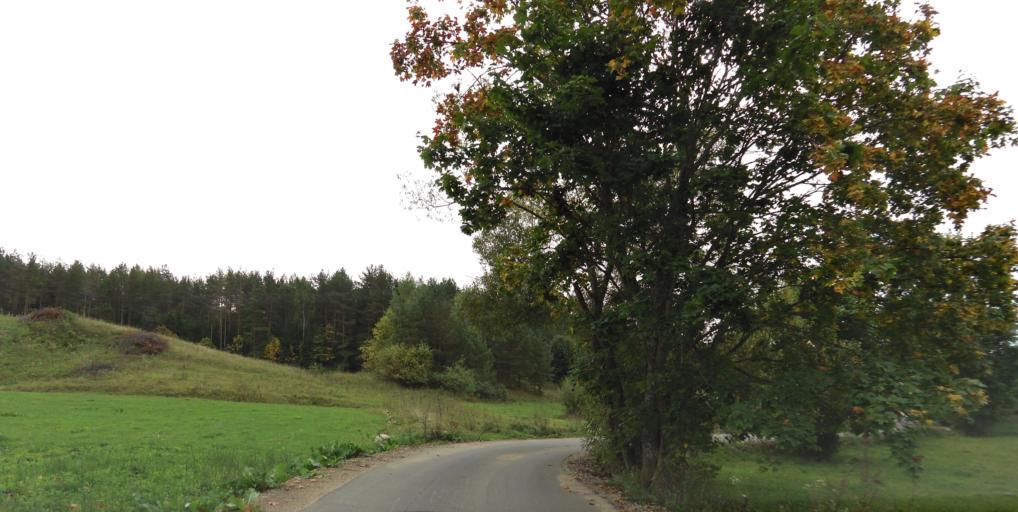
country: LT
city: Grigiskes
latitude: 54.7525
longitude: 25.0290
